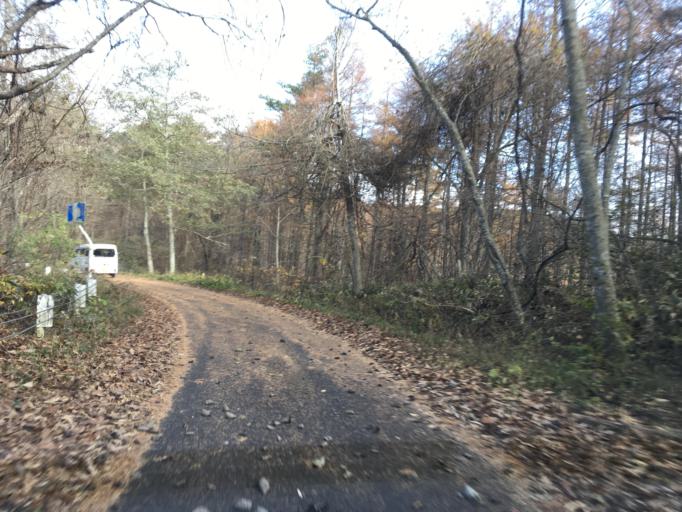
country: JP
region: Iwate
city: Mizusawa
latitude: 39.1288
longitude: 141.3028
